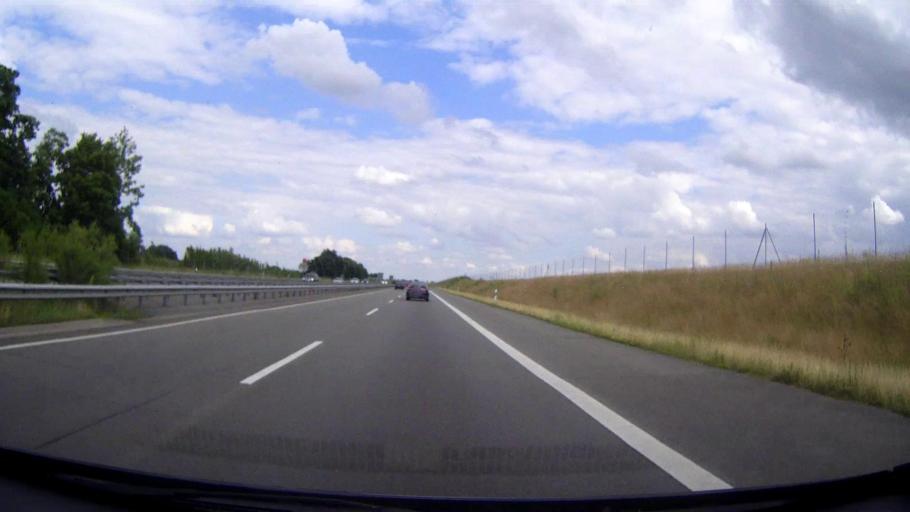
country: DE
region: Schleswig-Holstein
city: Weede
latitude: 53.9199
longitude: 10.3500
